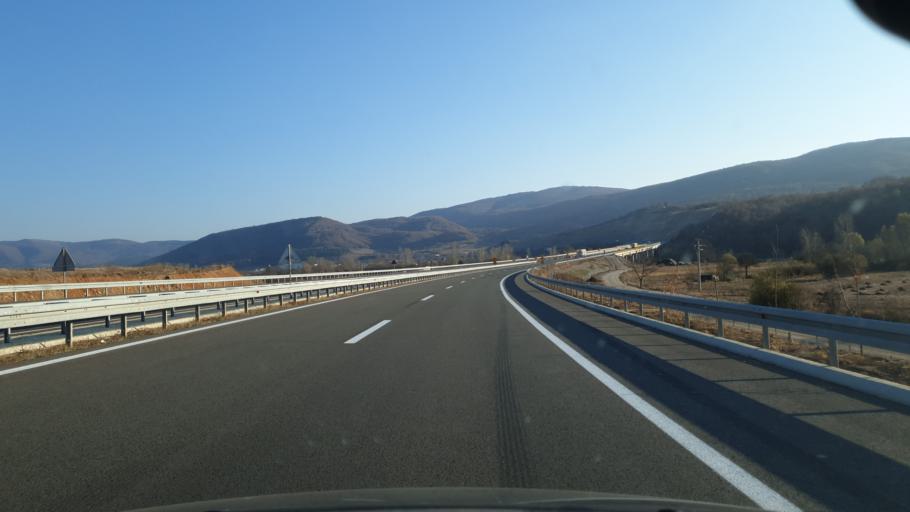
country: RS
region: Central Serbia
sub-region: Pirotski Okrug
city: Dimitrovgrad
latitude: 43.0149
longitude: 22.8016
